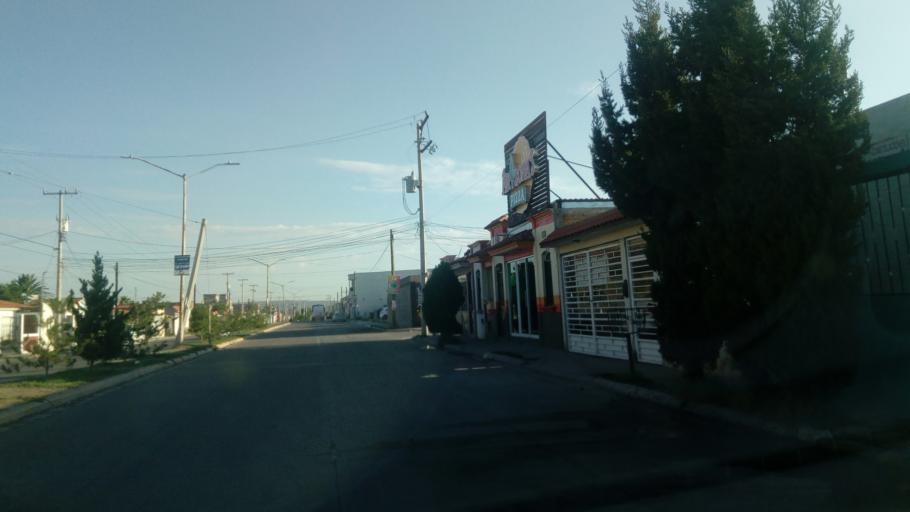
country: MX
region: Durango
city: Victoria de Durango
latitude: 24.0611
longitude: -104.5850
